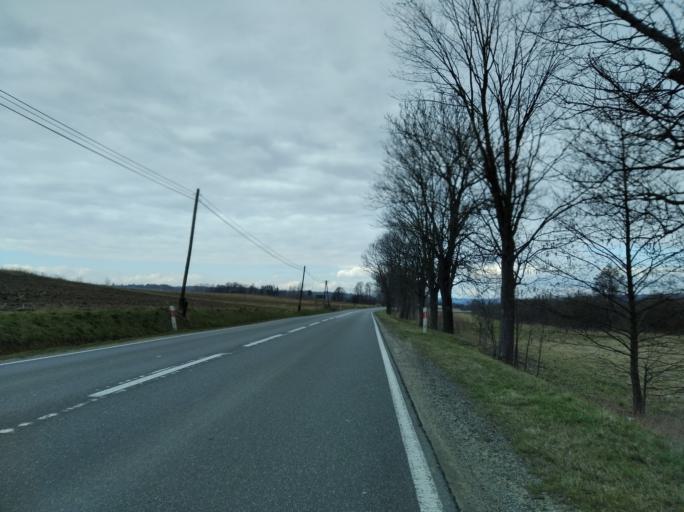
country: PL
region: Subcarpathian Voivodeship
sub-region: Powiat krosnienski
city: Wojaszowka
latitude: 49.7863
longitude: 21.6619
